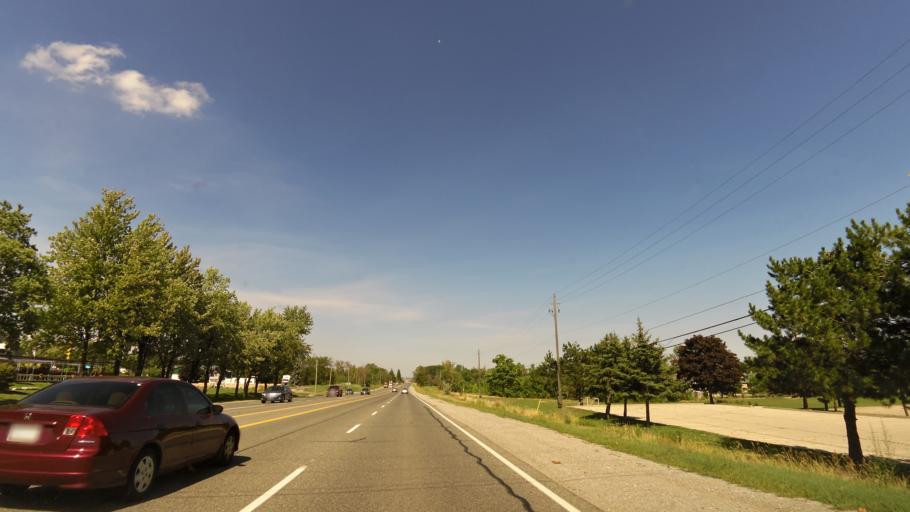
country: CA
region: Ontario
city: Burlington
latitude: 43.3694
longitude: -79.8491
